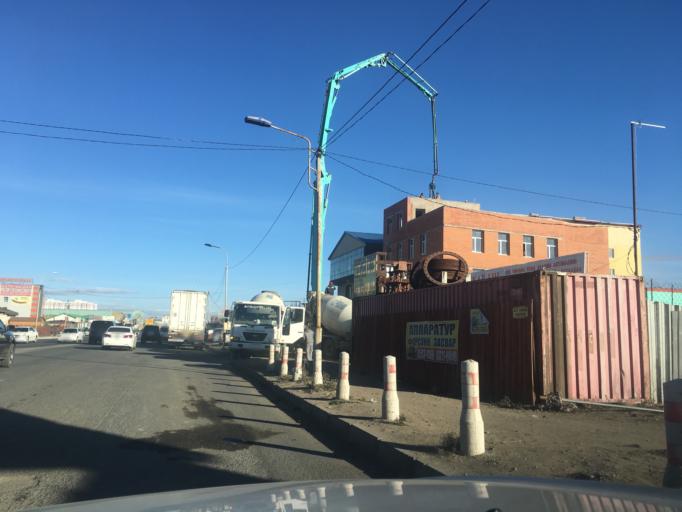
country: MN
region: Ulaanbaatar
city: Ulaanbaatar
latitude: 47.9076
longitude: 106.7888
